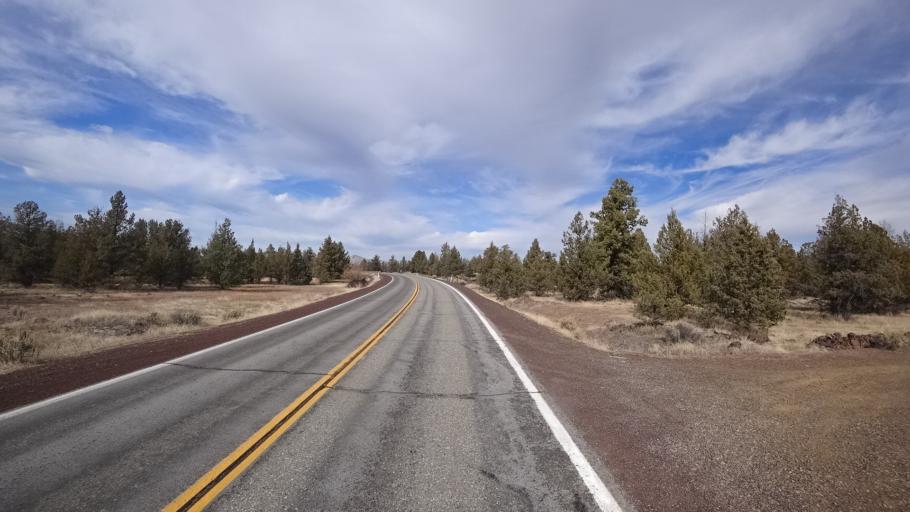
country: US
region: California
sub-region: Siskiyou County
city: Montague
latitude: 41.6045
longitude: -122.3944
